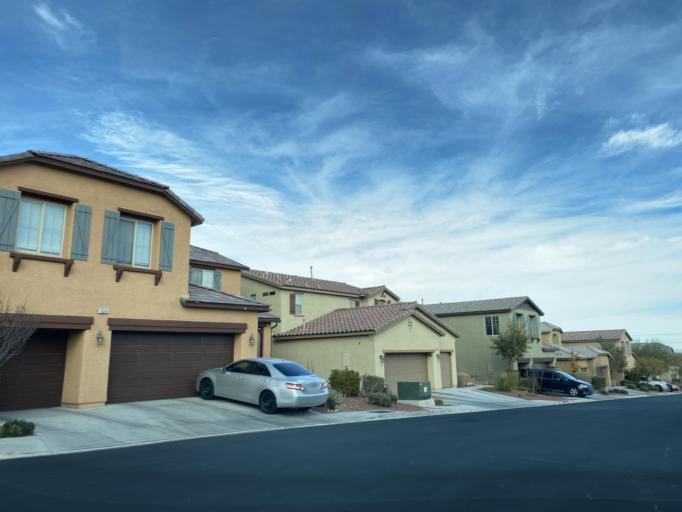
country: US
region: Nevada
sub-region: Clark County
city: Summerlin South
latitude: 36.2787
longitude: -115.3327
